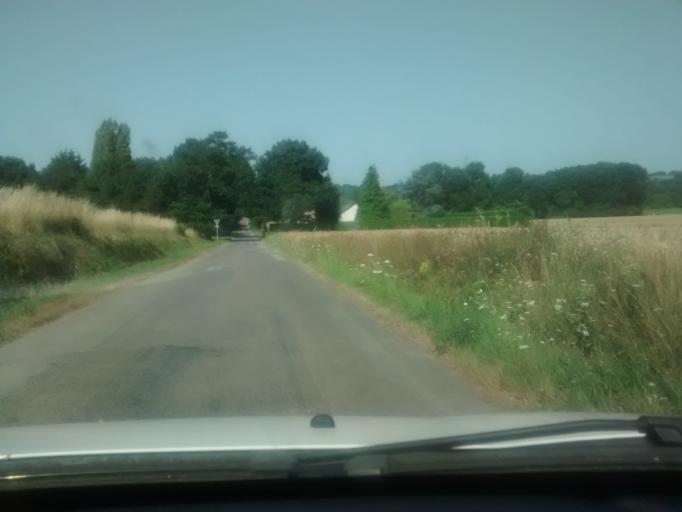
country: FR
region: Brittany
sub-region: Departement d'Ille-et-Vilaine
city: Cesson-Sevigne
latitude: 48.1315
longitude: -1.6001
